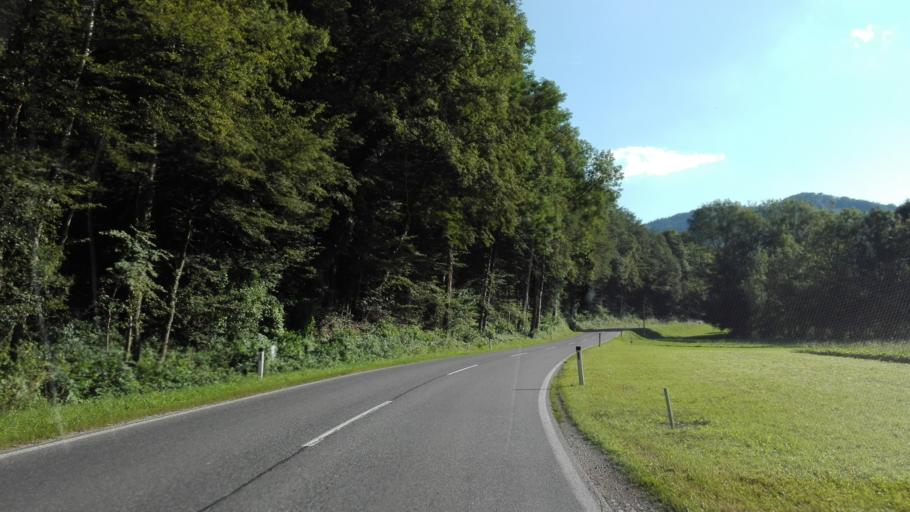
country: AT
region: Lower Austria
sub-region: Politischer Bezirk Sankt Polten
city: Stossing
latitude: 48.0897
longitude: 15.8712
